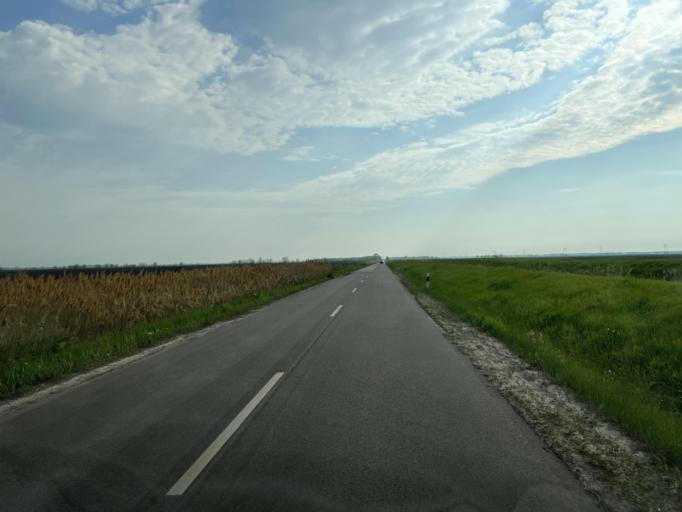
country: HU
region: Pest
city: Jaszkarajeno
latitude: 47.1079
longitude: 20.0455
